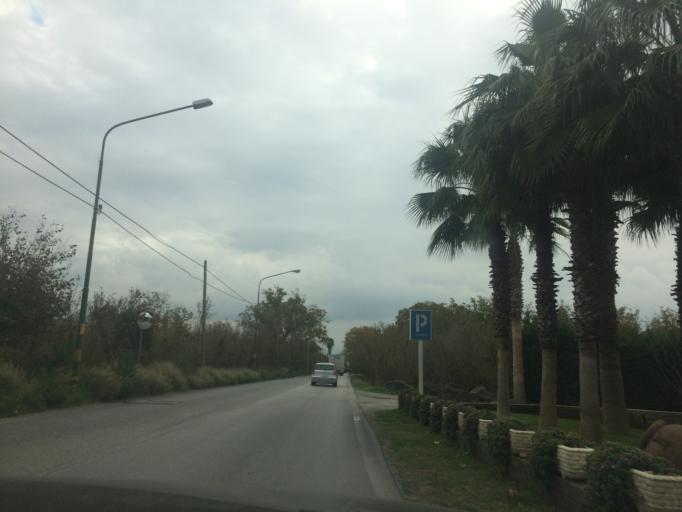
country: IT
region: Campania
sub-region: Provincia di Napoli
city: Piazzolla
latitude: 40.8924
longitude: 14.5316
